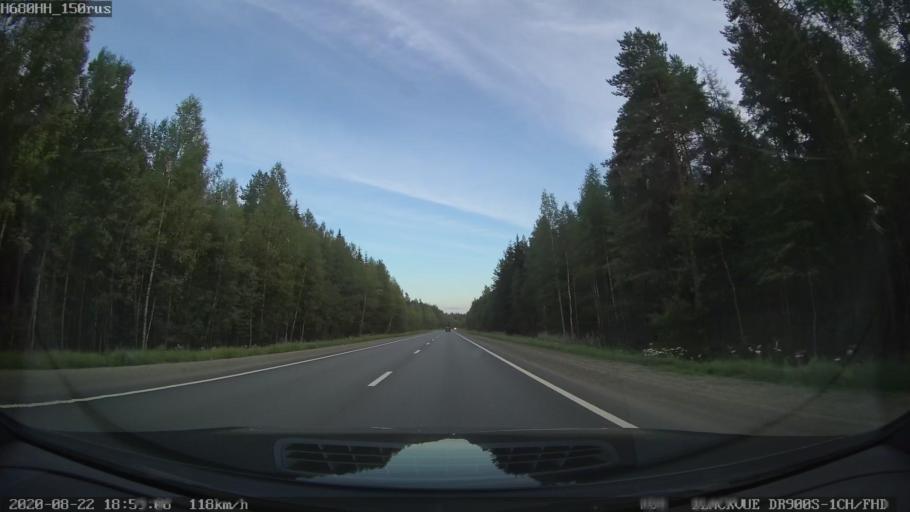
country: RU
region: Tverskaya
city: Rameshki
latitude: 57.1469
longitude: 36.0889
